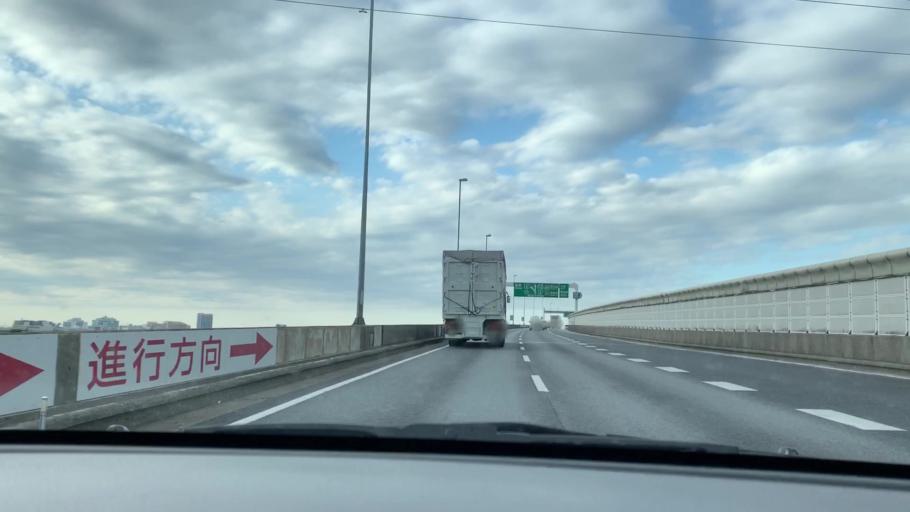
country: JP
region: Saitama
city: Yashio-shi
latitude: 35.7381
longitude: 139.8274
